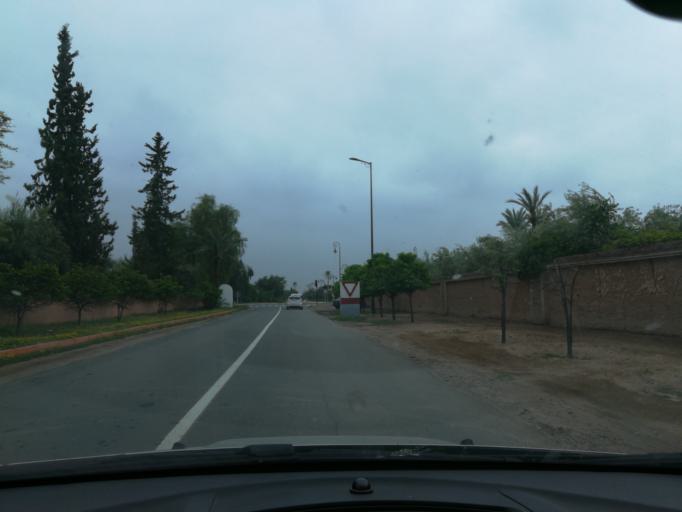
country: MA
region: Marrakech-Tensift-Al Haouz
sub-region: Marrakech
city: Marrakesh
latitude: 31.6476
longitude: -7.9730
